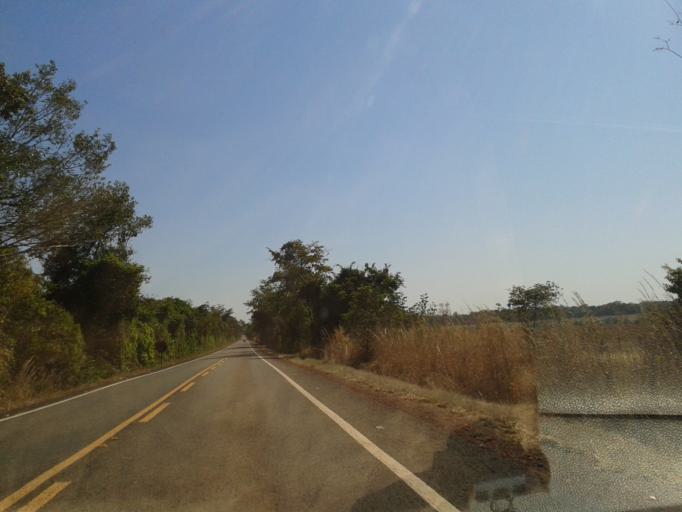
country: BR
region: Goias
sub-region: Sao Miguel Do Araguaia
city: Sao Miguel do Araguaia
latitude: -13.8375
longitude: -50.3386
